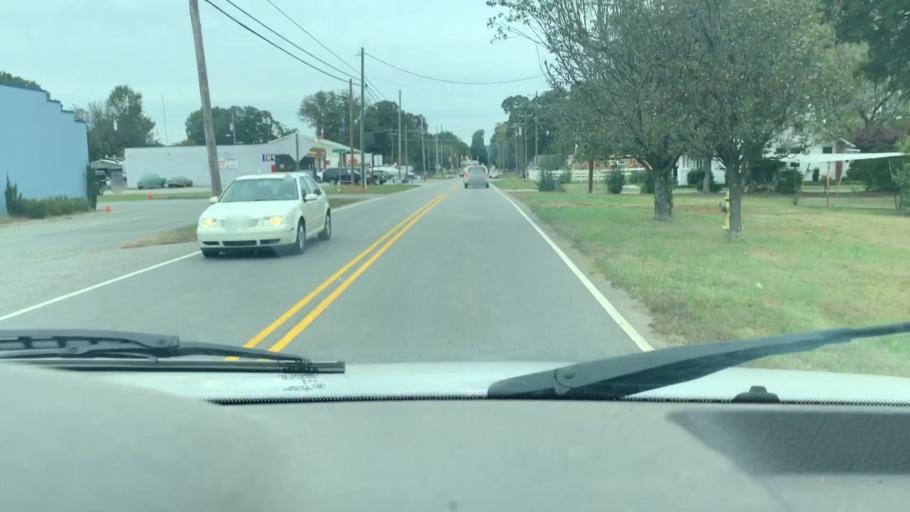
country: US
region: North Carolina
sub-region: Gaston County
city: Davidson
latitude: 35.5409
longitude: -80.8477
